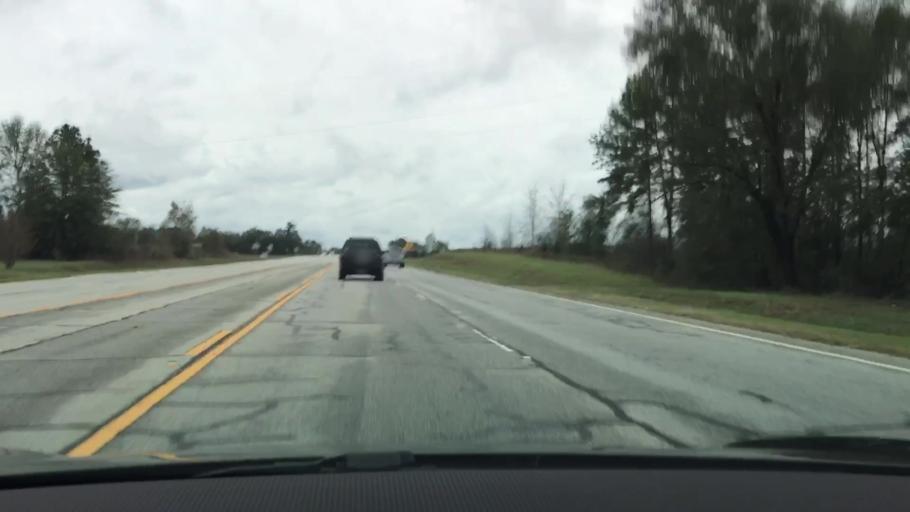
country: US
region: Georgia
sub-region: Jefferson County
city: Wadley
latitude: 32.8464
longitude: -82.3980
